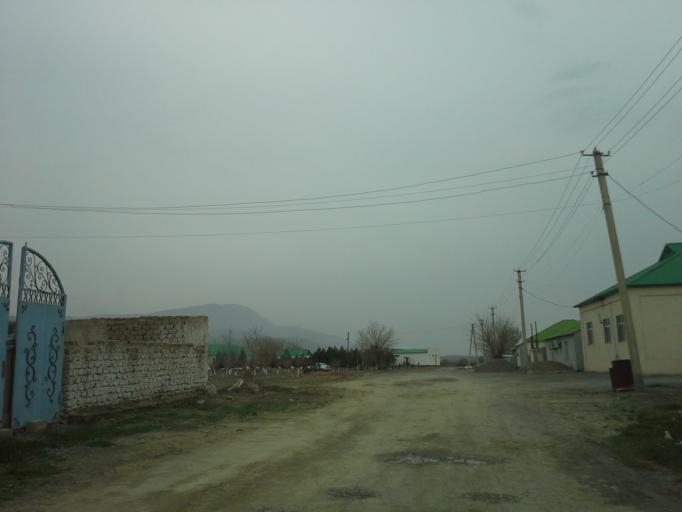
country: TM
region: Ahal
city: Abadan
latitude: 37.9807
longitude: 58.2186
